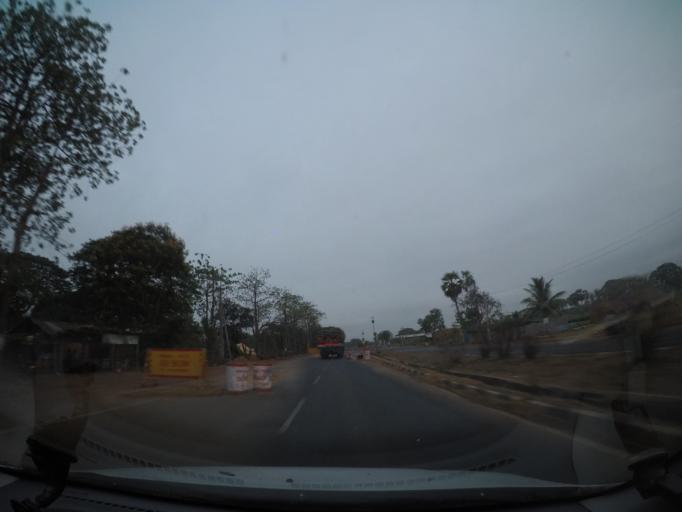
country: IN
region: Andhra Pradesh
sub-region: West Godavari
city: Eluru
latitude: 16.8044
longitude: 81.3005
